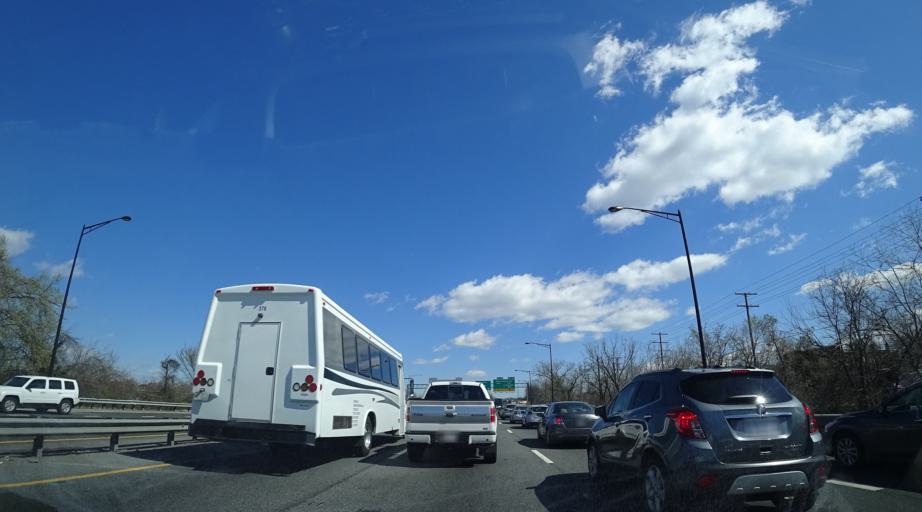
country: US
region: Maryland
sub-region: Prince George's County
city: Hillcrest Heights
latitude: 38.8734
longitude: -76.9791
